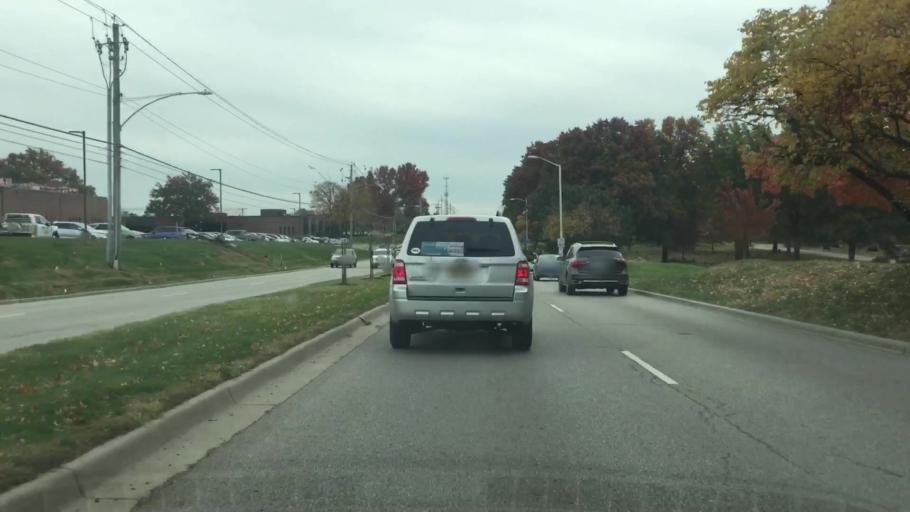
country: US
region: Kansas
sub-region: Johnson County
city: Lenexa
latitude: 38.9778
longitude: -94.7237
